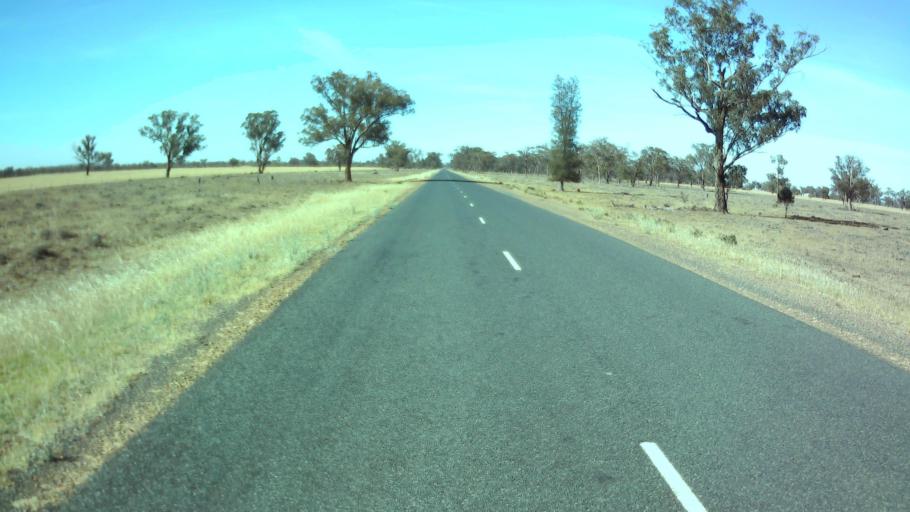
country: AU
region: New South Wales
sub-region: Weddin
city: Grenfell
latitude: -34.0836
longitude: 147.8942
